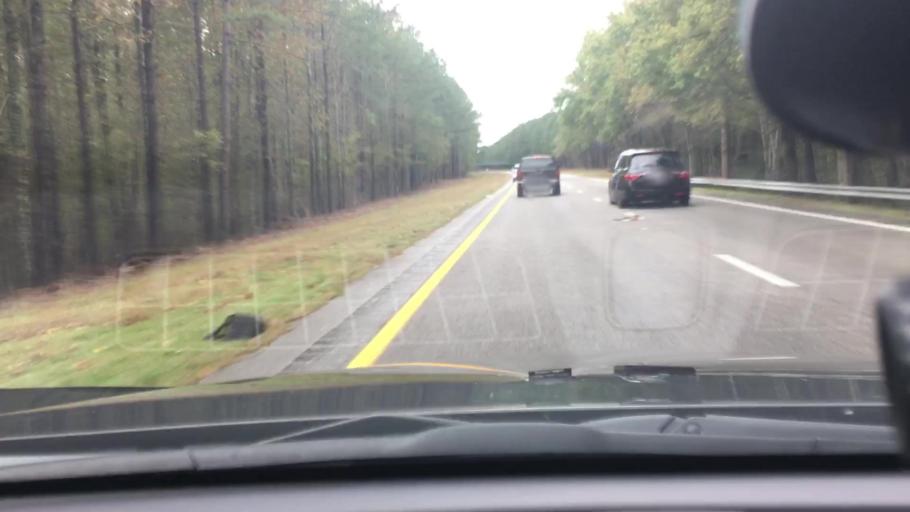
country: US
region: North Carolina
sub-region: Nash County
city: Spring Hope
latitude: 35.7921
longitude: -78.1469
